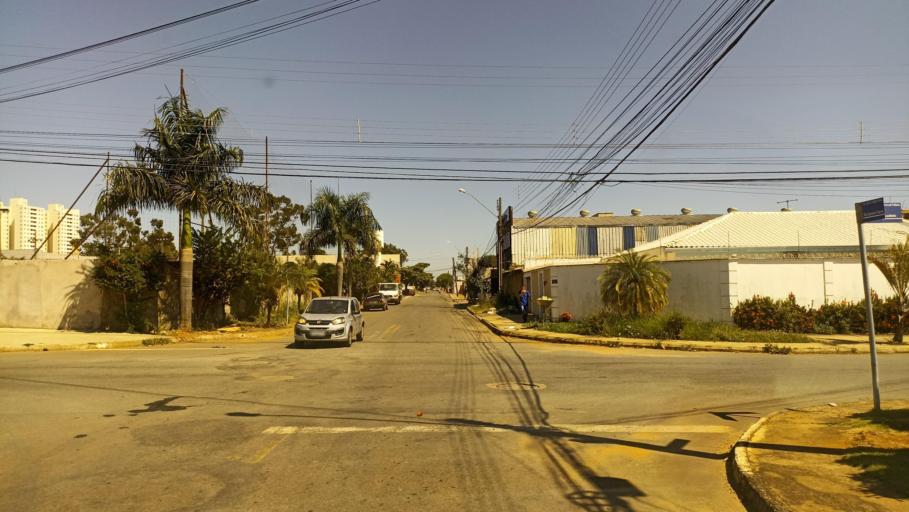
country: BR
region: Goias
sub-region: Goiania
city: Goiania
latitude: -16.7018
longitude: -49.3248
